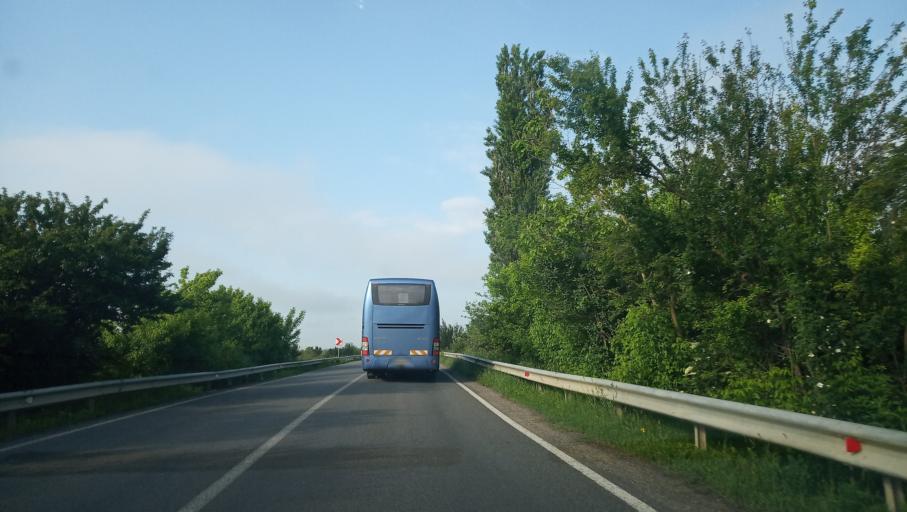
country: RO
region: Timis
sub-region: Comuna Moravita
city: Moravita
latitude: 45.2523
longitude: 21.2671
